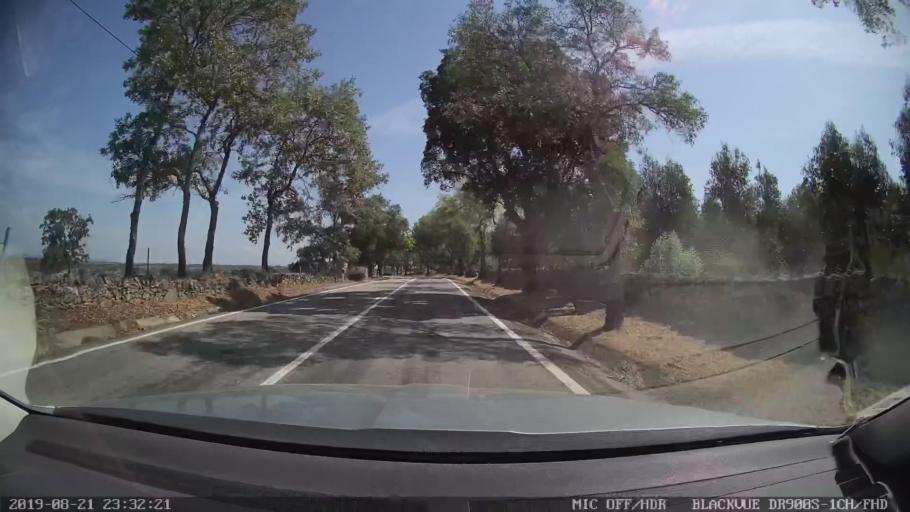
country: PT
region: Guarda
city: Alcains
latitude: 39.8777
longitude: -7.4141
